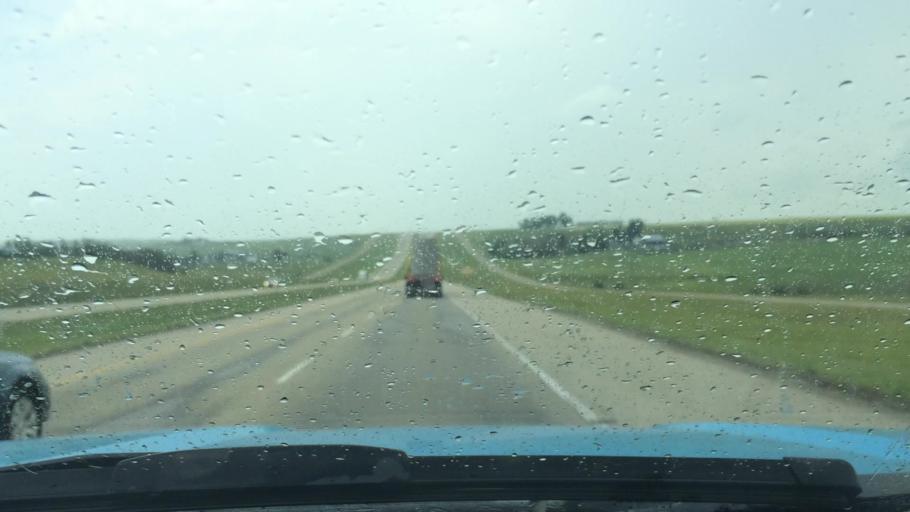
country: CA
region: Alberta
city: Carstairs
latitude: 51.5439
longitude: -114.0250
